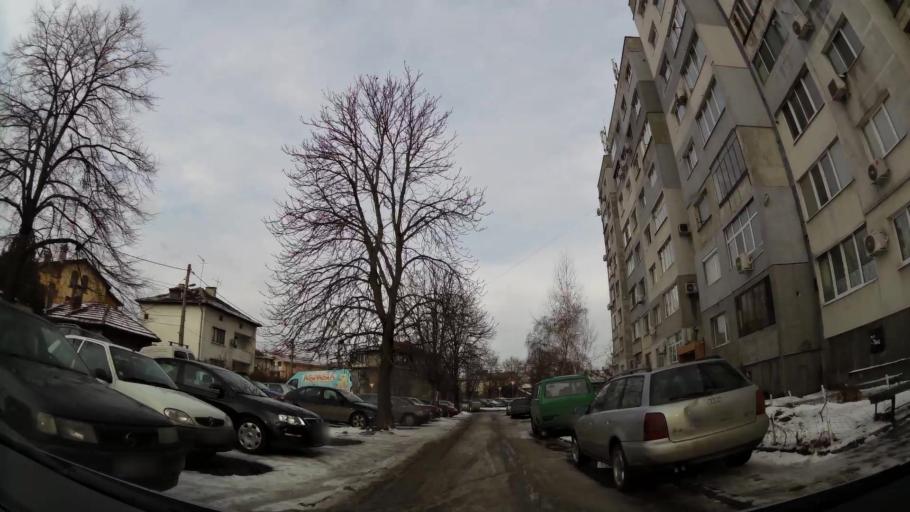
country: BG
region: Sofia-Capital
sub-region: Stolichna Obshtina
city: Sofia
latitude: 42.7146
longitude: 23.3433
